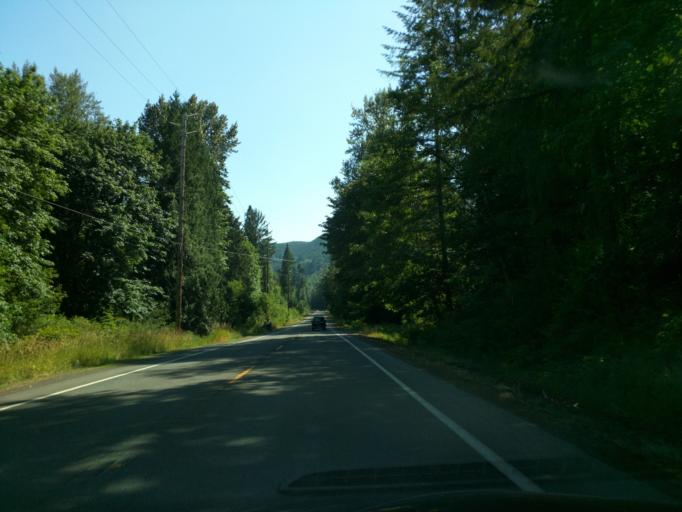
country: US
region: Washington
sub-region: Whatcom County
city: Peaceful Valley
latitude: 48.8875
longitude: -122.1530
